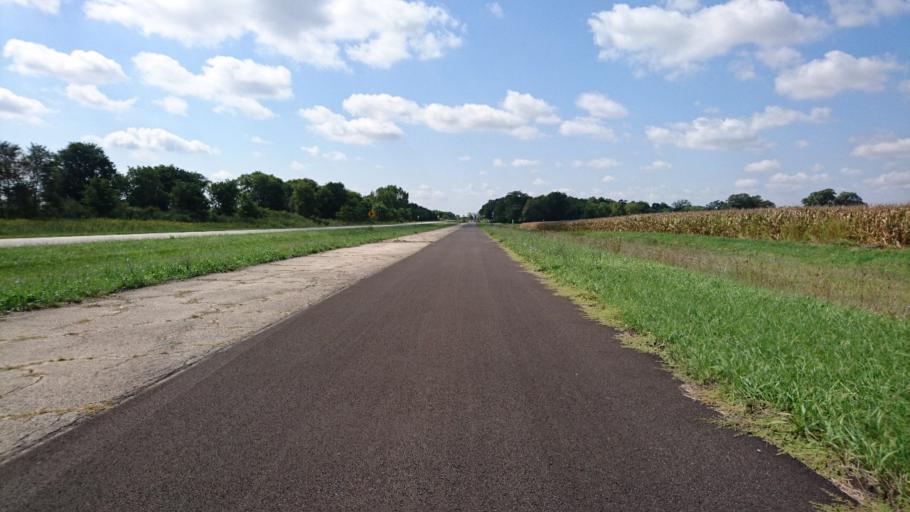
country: US
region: Illinois
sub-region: McLean County
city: Lexington
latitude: 40.5848
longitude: -88.8677
